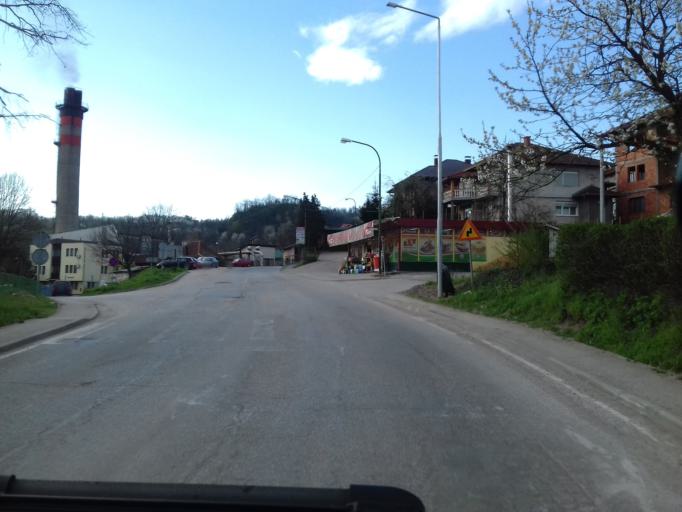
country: BA
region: Federation of Bosnia and Herzegovina
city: Tesanj
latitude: 44.6219
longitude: 17.9963
